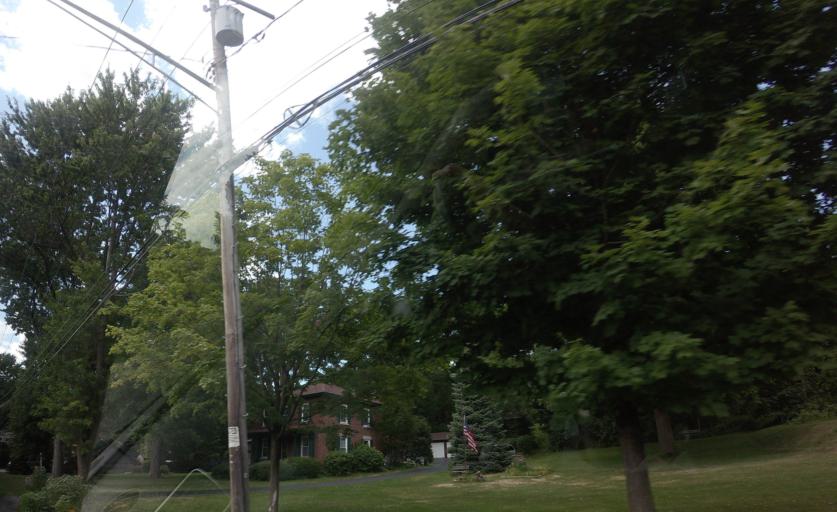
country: US
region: New York
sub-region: Onondaga County
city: Westvale
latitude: 43.0471
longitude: -76.2174
